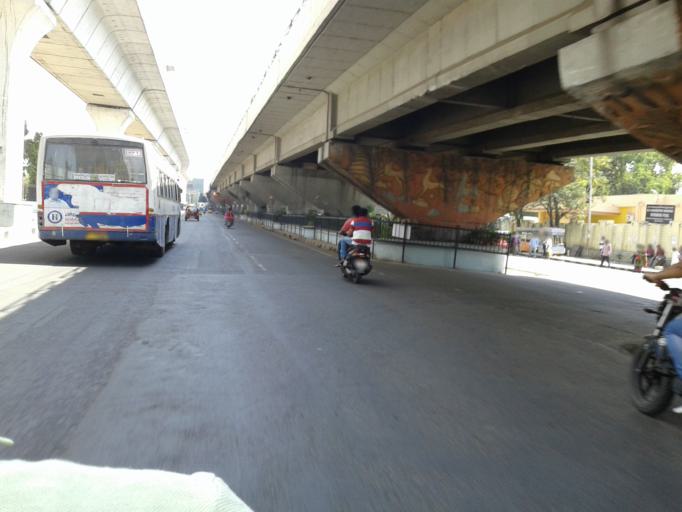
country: IN
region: Telangana
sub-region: Hyderabad
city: Malkajgiri
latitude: 17.4432
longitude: 78.4938
